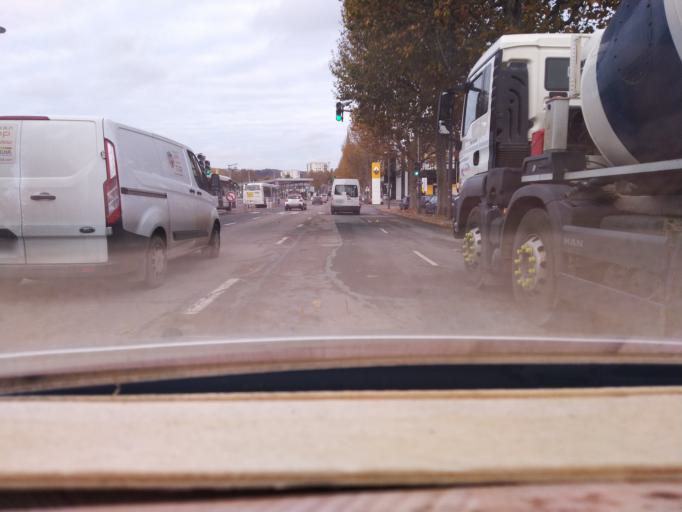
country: FR
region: Haute-Normandie
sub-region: Departement de la Seine-Maritime
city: Deville-les-Rouen
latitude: 49.4480
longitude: 1.0674
